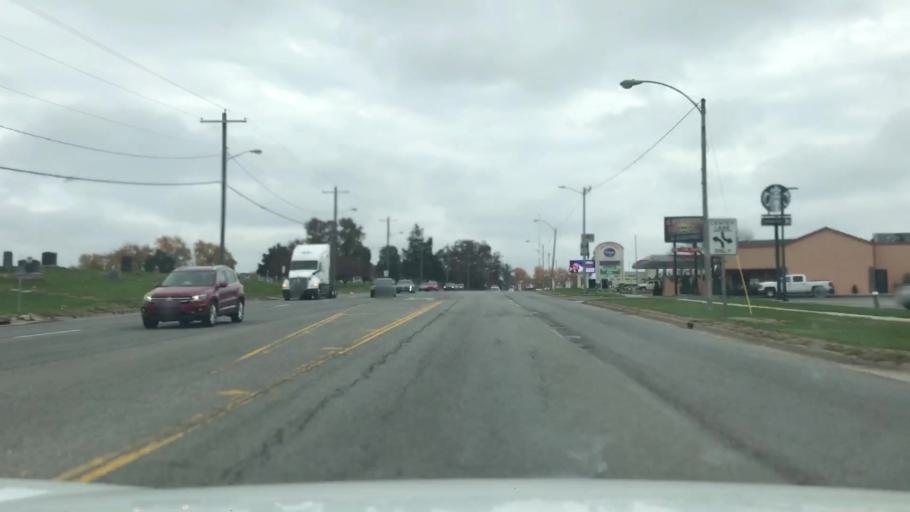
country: US
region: Illinois
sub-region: Jefferson County
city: Mount Vernon
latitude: 38.3132
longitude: -88.9467
